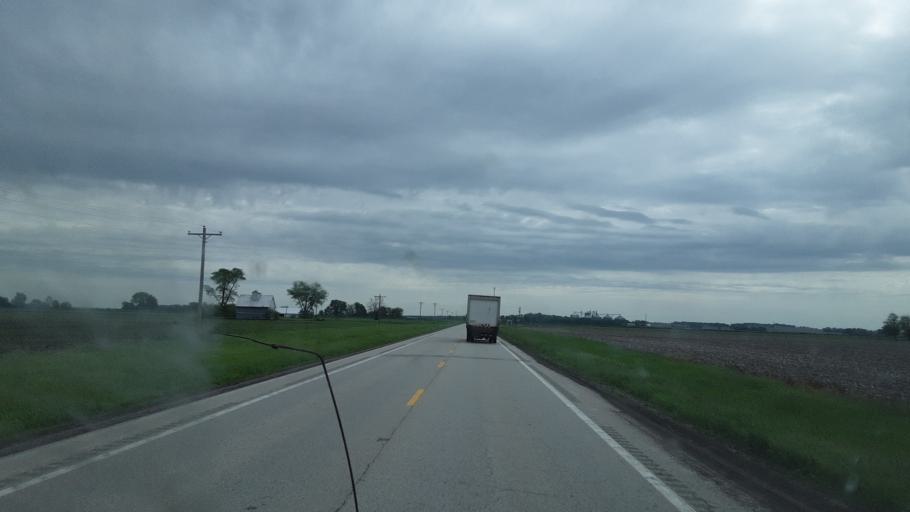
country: US
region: Illinois
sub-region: Mason County
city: Mason City
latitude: 40.3048
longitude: -89.6824
